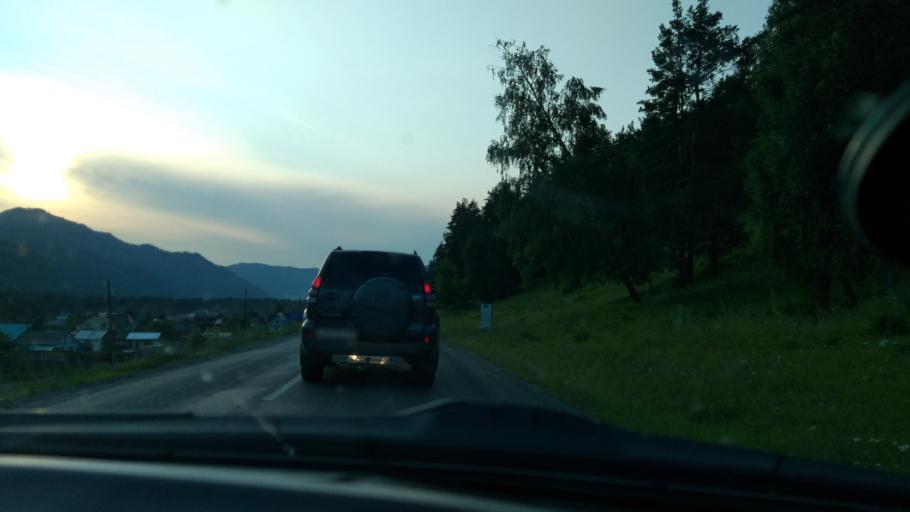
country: RU
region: Altay
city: Elekmonar
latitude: 51.5897
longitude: 85.8330
